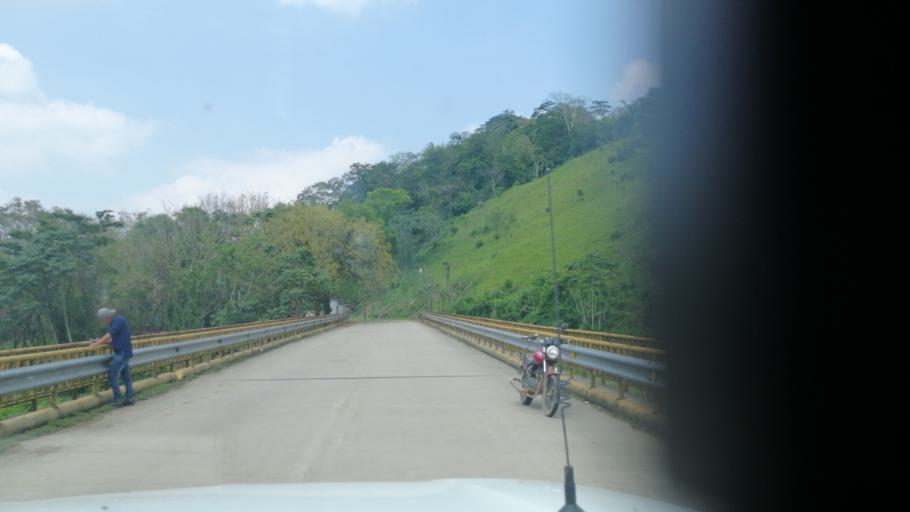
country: MX
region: Chiapas
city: Ostuacan
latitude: 17.4020
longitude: -93.3331
